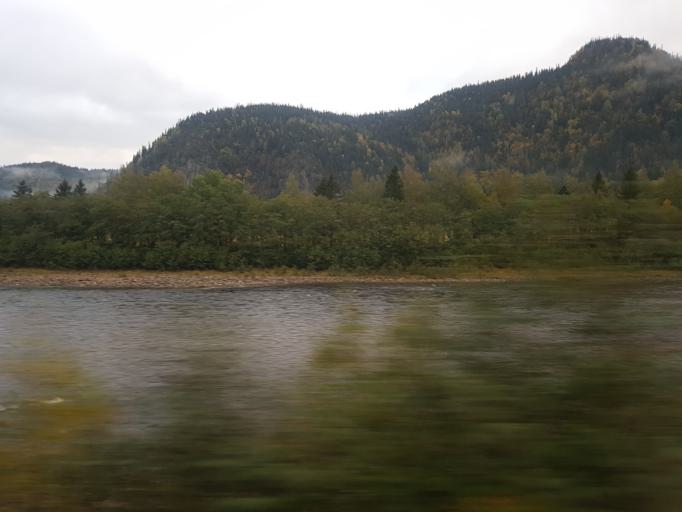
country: NO
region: Sor-Trondelag
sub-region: Midtre Gauldal
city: Storen
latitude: 63.0747
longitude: 10.2570
